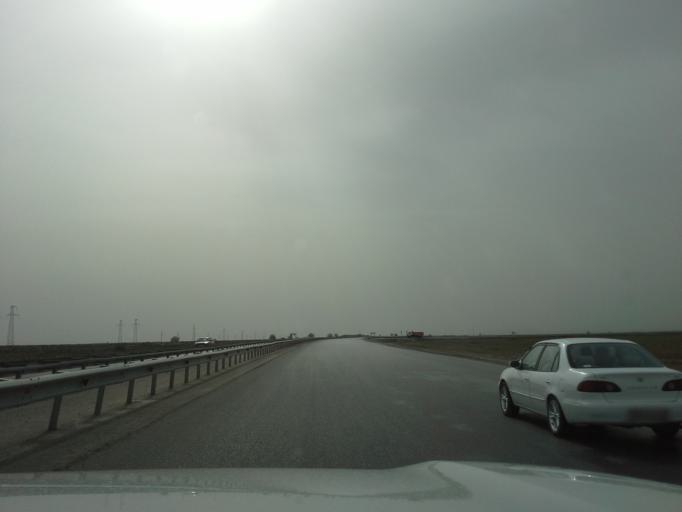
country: TM
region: Ahal
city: Kaka
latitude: 37.4761
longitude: 59.4915
